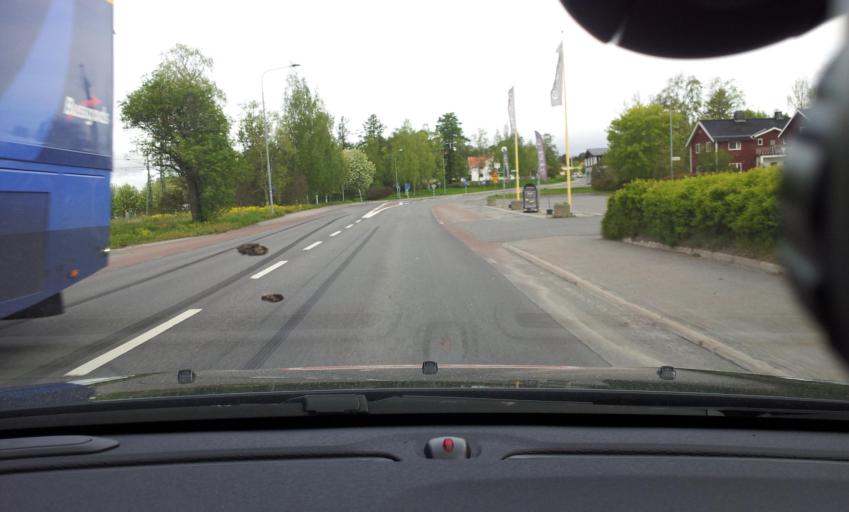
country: SE
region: Jaemtland
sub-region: OEstersunds Kommun
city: Brunflo
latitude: 63.0777
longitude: 14.8296
